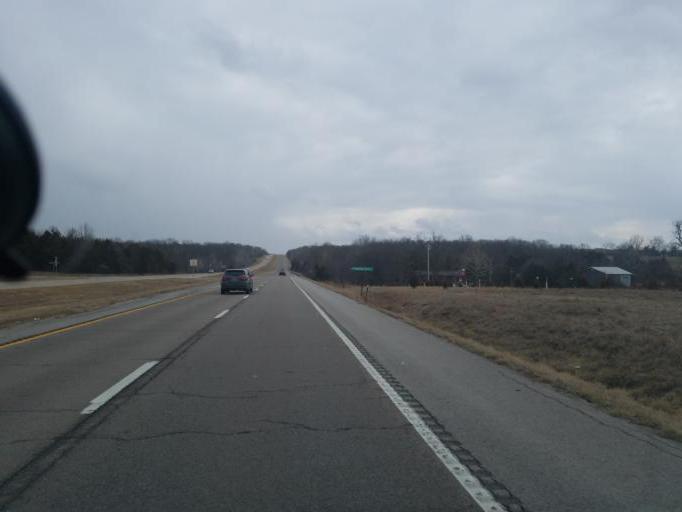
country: US
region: Missouri
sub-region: Boone County
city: Hallsville
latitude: 39.1076
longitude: -92.3292
